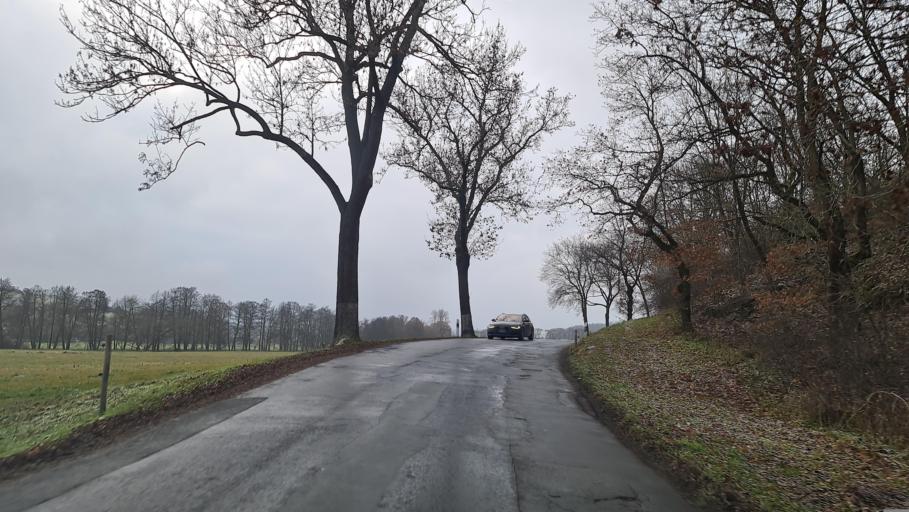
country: DE
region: Saxony
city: Weischlitz
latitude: 50.4738
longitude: 12.0797
